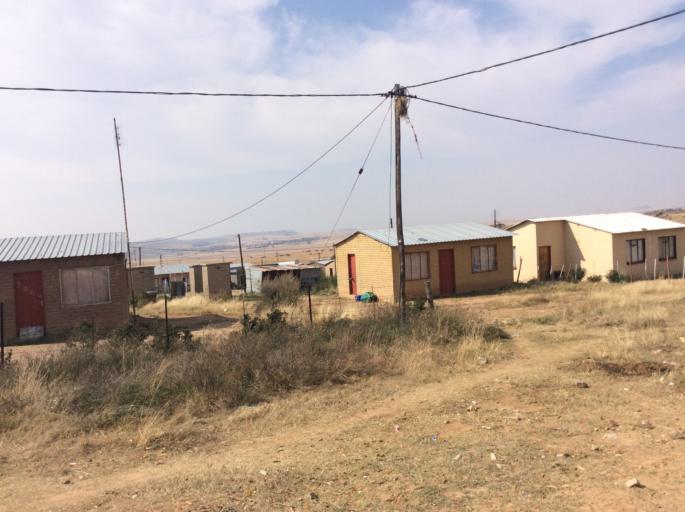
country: ZA
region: Orange Free State
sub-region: Xhariep District Municipality
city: Dewetsdorp
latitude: -29.5971
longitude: 26.6801
